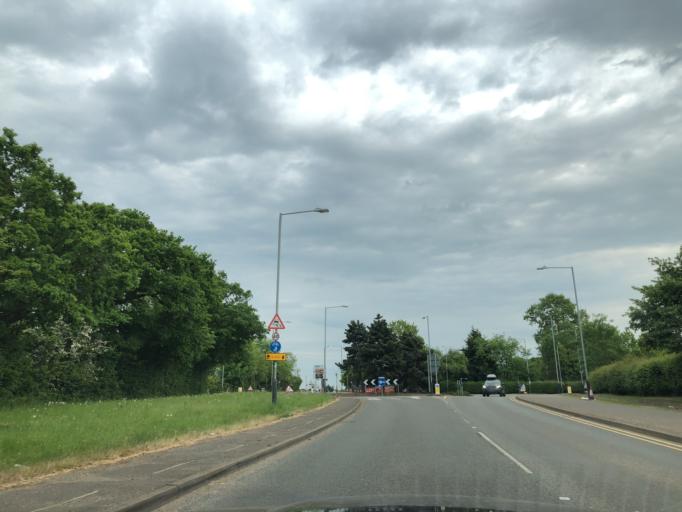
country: GB
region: England
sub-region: Warwickshire
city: Harbury
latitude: 52.1952
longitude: -1.4789
